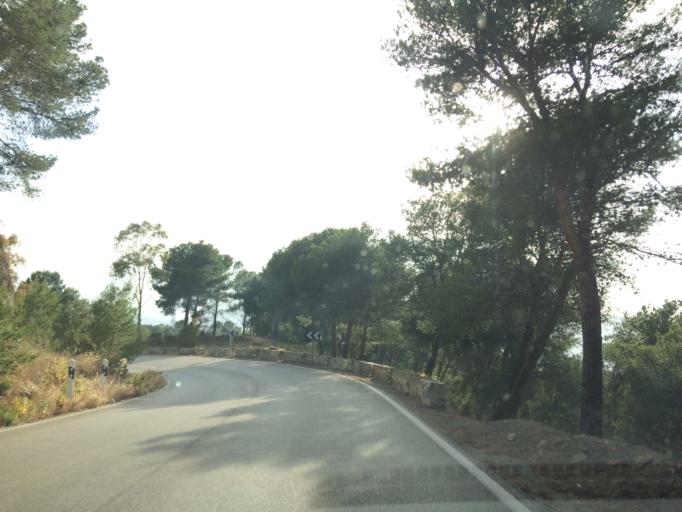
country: ES
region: Andalusia
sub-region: Provincia de Malaga
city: Malaga
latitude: 36.7683
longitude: -4.3982
